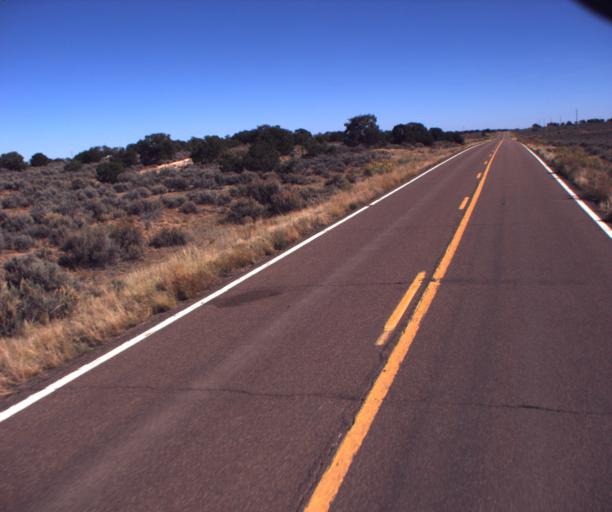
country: US
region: Arizona
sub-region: Apache County
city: Ganado
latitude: 35.7485
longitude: -109.9303
